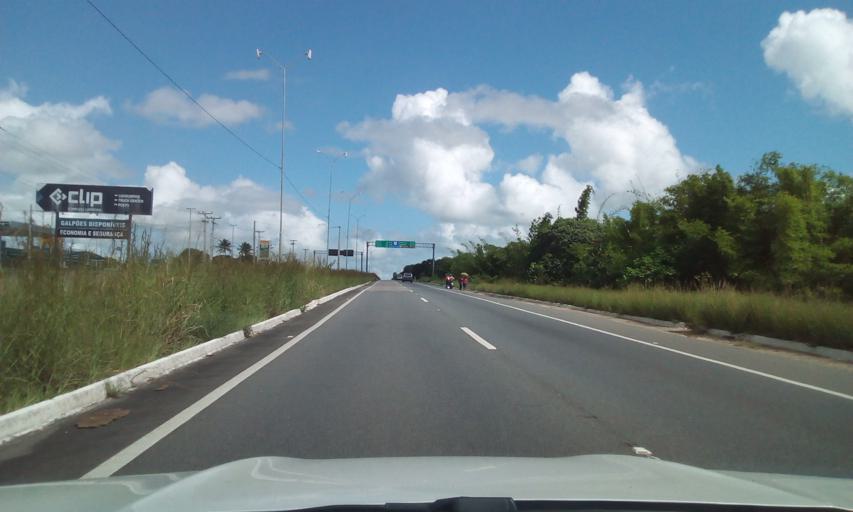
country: BR
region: Paraiba
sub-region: Conde
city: Conde
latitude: -7.2711
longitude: -34.9377
